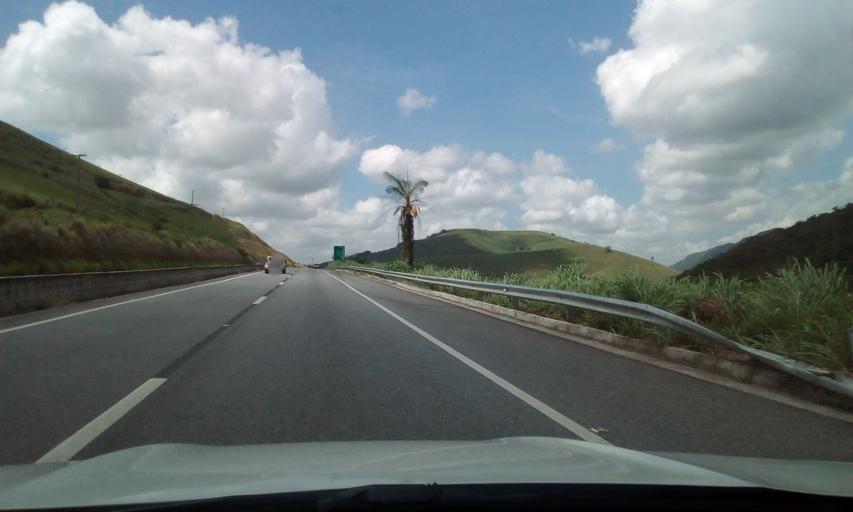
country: BR
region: Alagoas
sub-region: Flexeiras
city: Flexeiras
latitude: -9.2504
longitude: -35.7682
